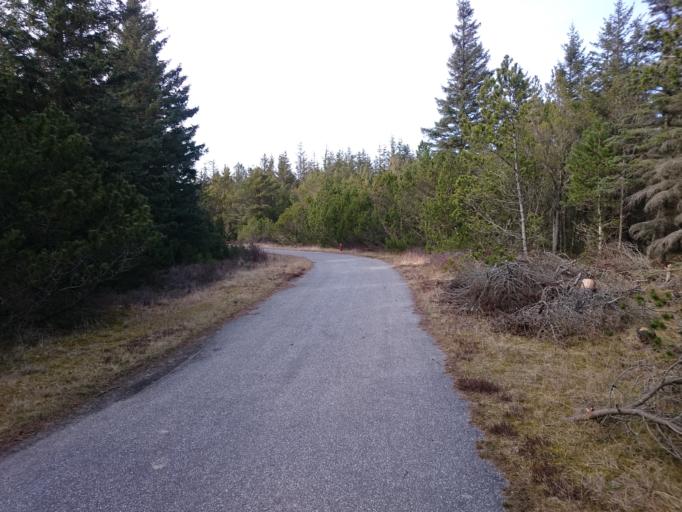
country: DK
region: North Denmark
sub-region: Frederikshavn Kommune
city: Skagen
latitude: 57.6981
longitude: 10.5211
